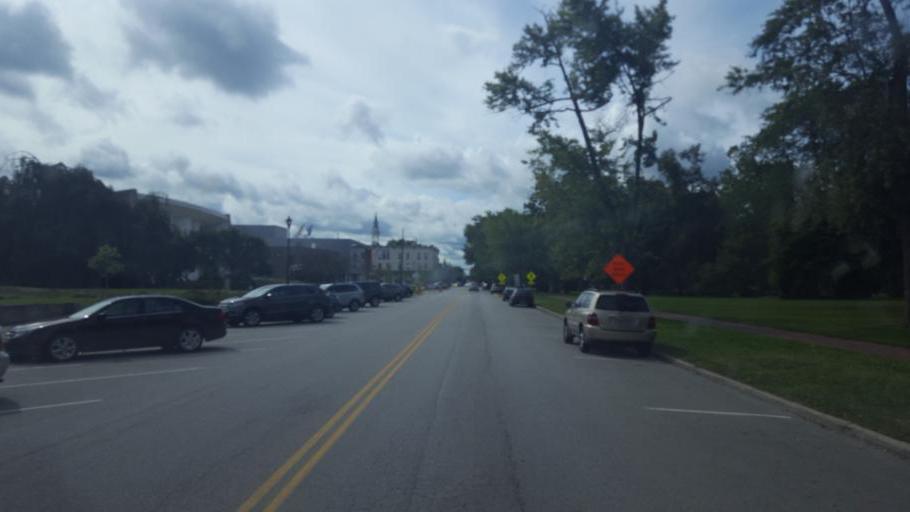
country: US
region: Ohio
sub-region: Lorain County
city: Oberlin
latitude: 41.2937
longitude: -82.2173
